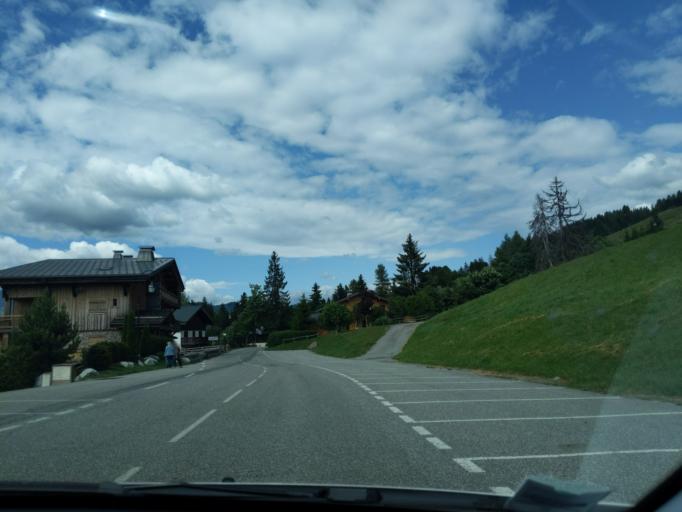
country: FR
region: Rhone-Alpes
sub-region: Departement de la Haute-Savoie
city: Praz-sur-Arly
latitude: 45.7852
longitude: 6.5007
